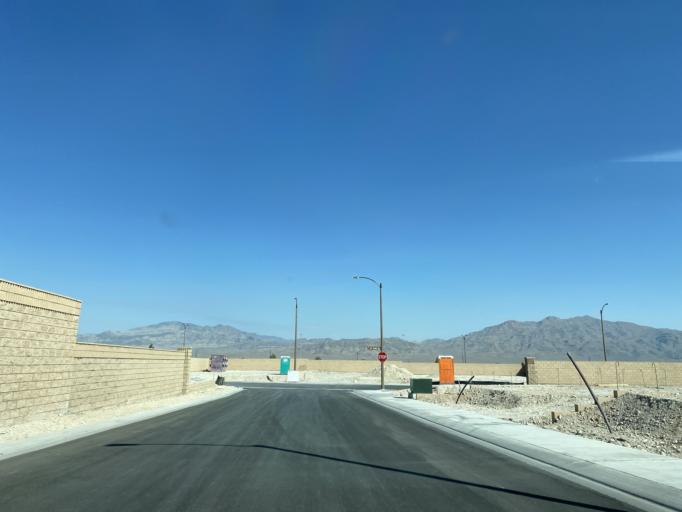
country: US
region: Nevada
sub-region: Clark County
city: Summerlin South
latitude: 36.3192
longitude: -115.3103
